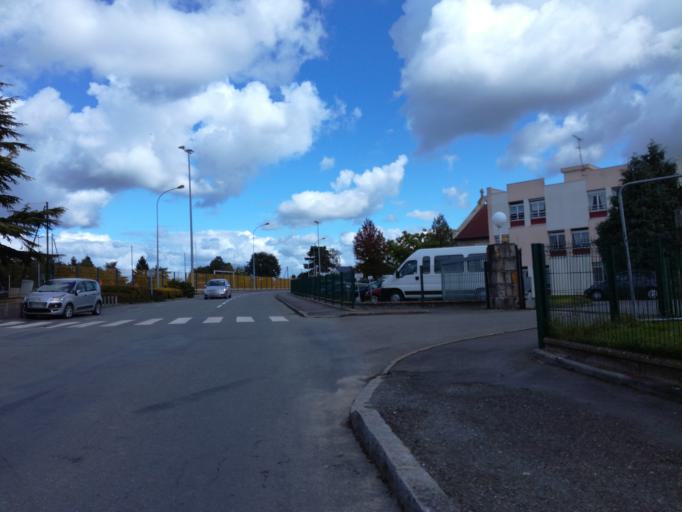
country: FR
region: Brittany
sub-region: Departement d'Ille-et-Vilaine
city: Saint-Aubin-du-Cormier
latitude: 48.2576
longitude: -1.4042
